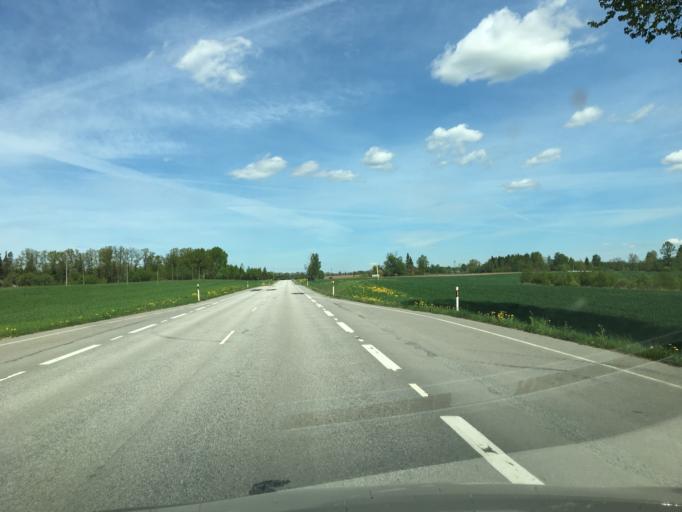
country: EE
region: Vorumaa
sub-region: Antsla vald
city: Vana-Antsla
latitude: 57.8922
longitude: 26.2886
